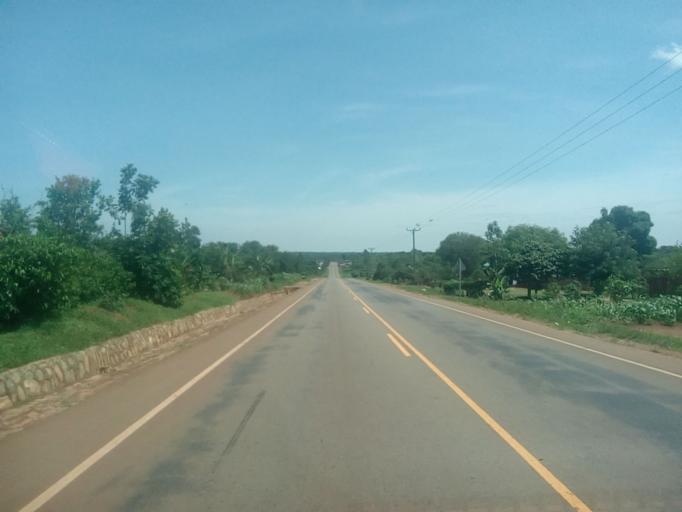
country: UG
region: Eastern Region
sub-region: Kamuli District
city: Kamuli
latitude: 0.8450
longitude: 33.1296
